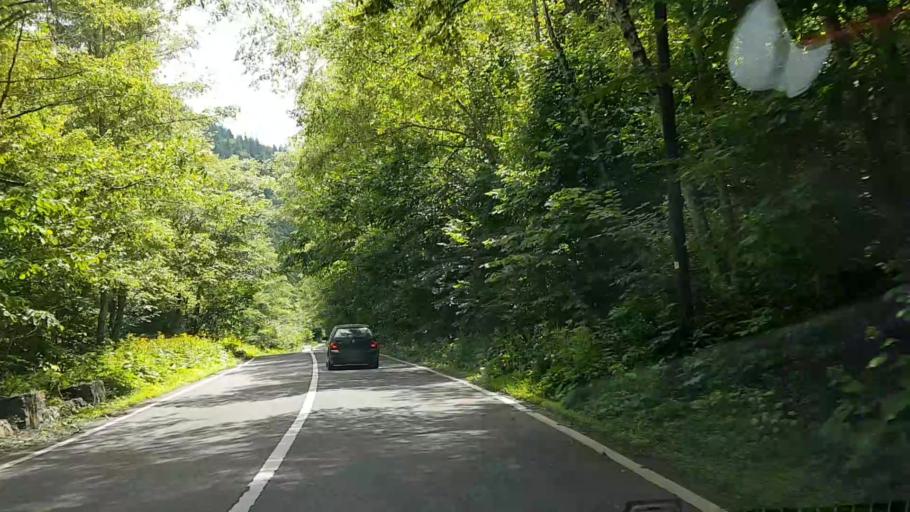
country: RO
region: Suceava
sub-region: Comuna Crucea
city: Crucea
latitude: 47.3031
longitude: 25.6286
